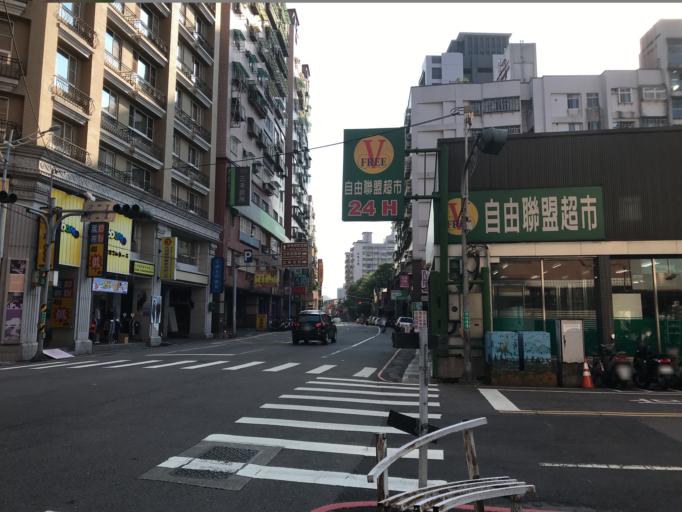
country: TW
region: Taiwan
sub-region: Taoyuan
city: Taoyuan
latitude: 24.9325
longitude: 121.3740
